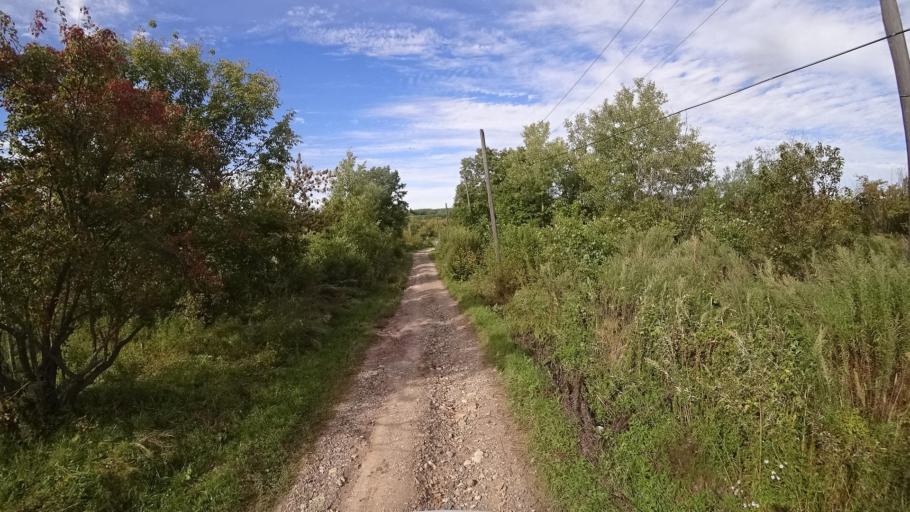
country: RU
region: Primorskiy
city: Dostoyevka
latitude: 44.3270
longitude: 133.4867
